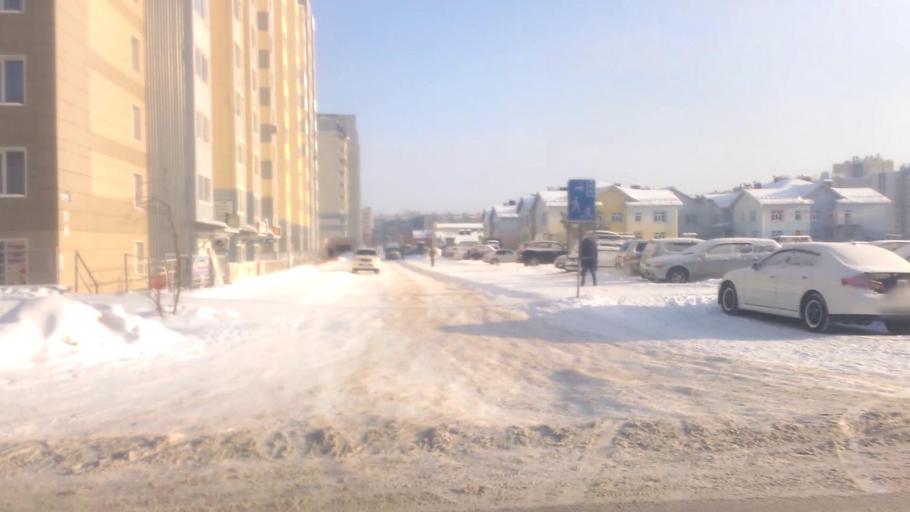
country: RU
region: Altai Krai
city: Novosilikatnyy
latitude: 53.3441
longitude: 83.6556
